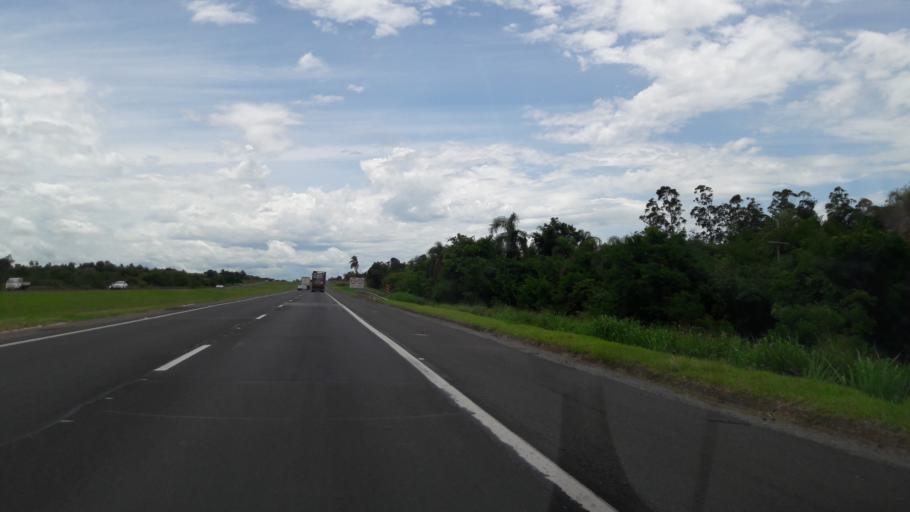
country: BR
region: Sao Paulo
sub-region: Porangaba
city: Porangaba
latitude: -23.2487
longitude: -48.0002
